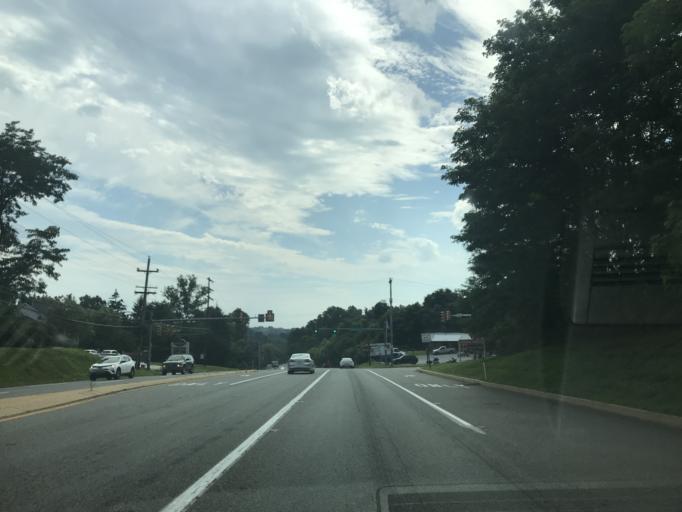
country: US
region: Pennsylvania
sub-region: Delaware County
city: Chester Heights
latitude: 39.8794
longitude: -75.5509
